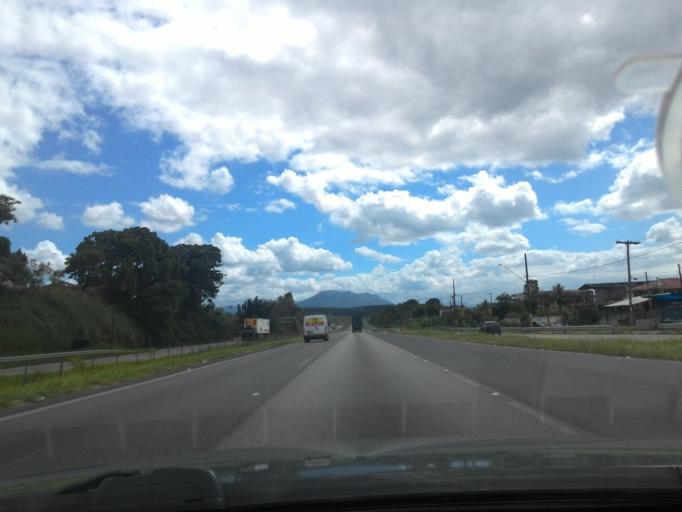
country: BR
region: Sao Paulo
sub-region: Jacupiranga
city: Jacupiranga
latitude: -24.7023
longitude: -48.0089
